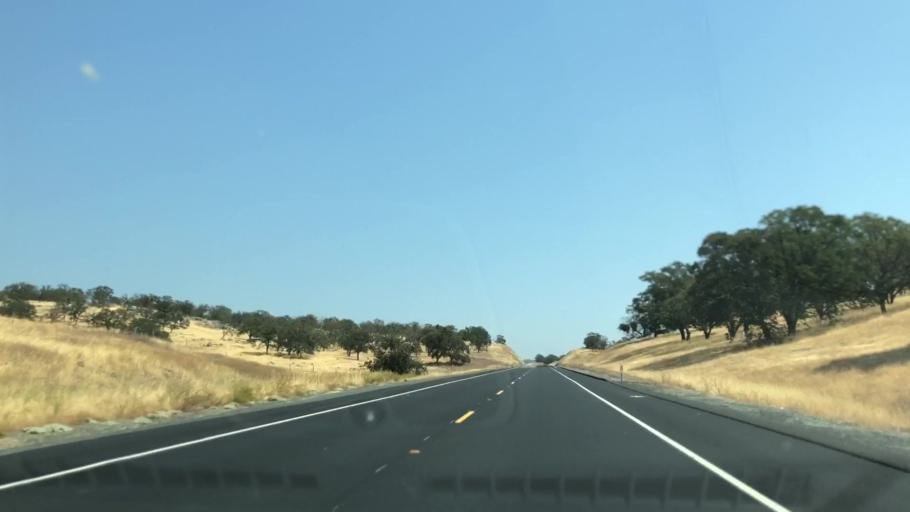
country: US
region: California
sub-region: Calaveras County
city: Copperopolis
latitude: 37.9404
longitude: -120.7487
